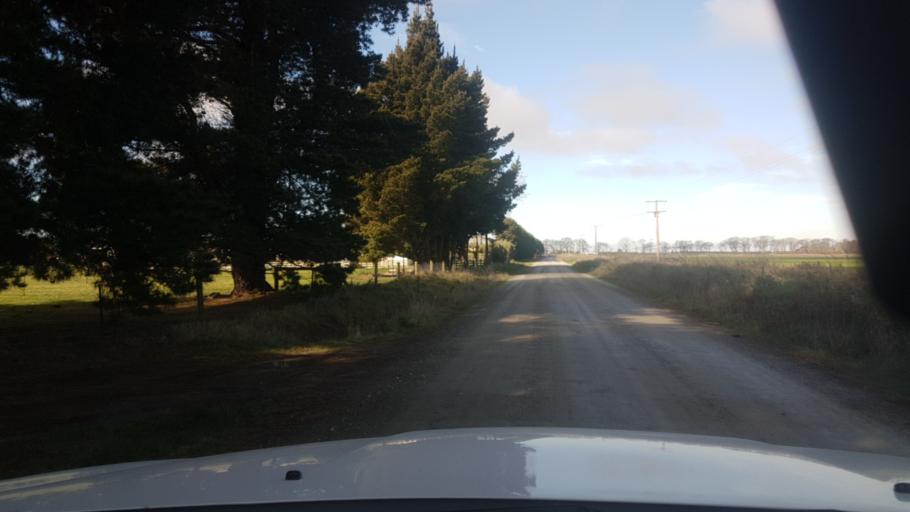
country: NZ
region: Canterbury
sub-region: Timaru District
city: Timaru
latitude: -44.3281
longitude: 171.2445
